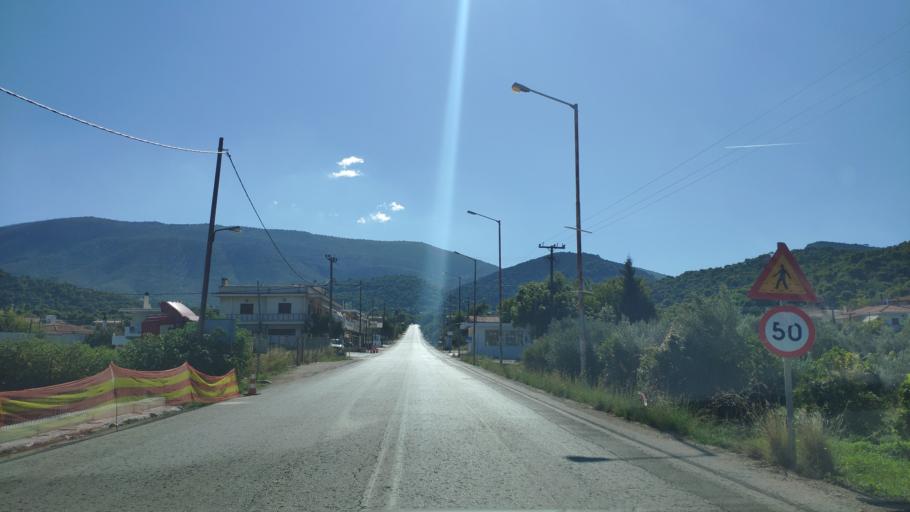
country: GR
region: Peloponnese
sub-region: Nomos Korinthias
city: Loutra Oraias Elenis
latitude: 37.8465
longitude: 23.0010
